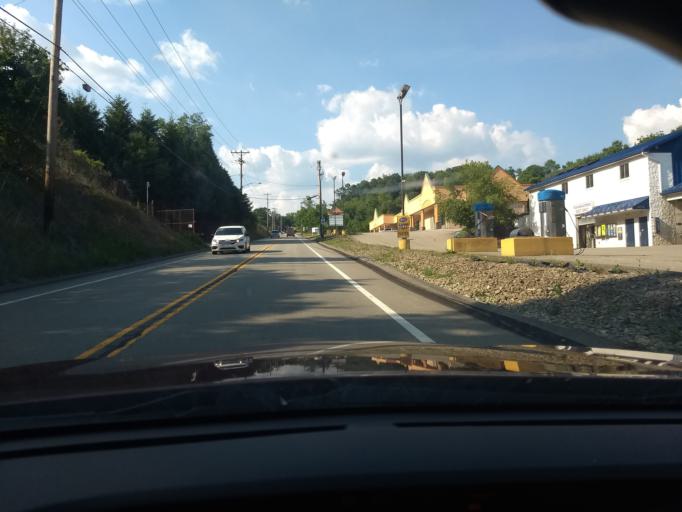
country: US
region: Pennsylvania
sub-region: Allegheny County
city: East McKeesport
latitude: 40.3612
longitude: -79.7855
